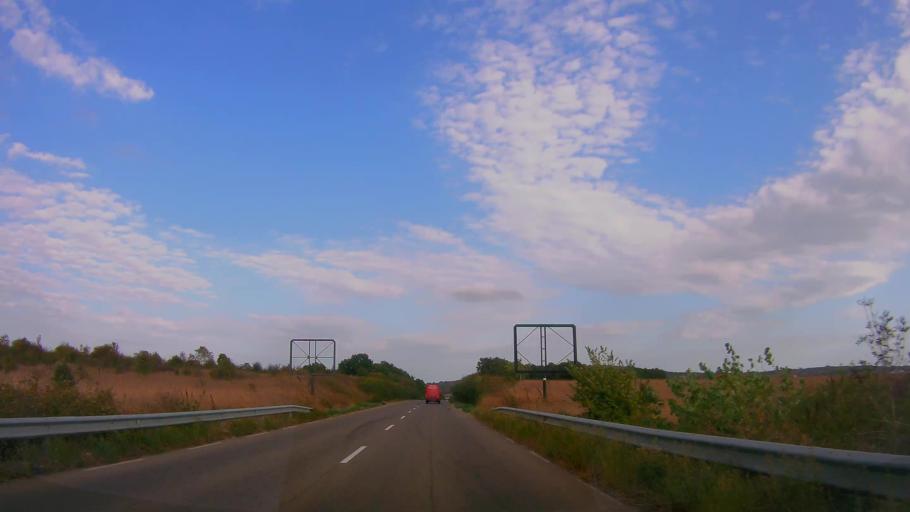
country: BG
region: Burgas
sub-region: Obshtina Sozopol
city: Sozopol
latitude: 42.3557
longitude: 27.7056
